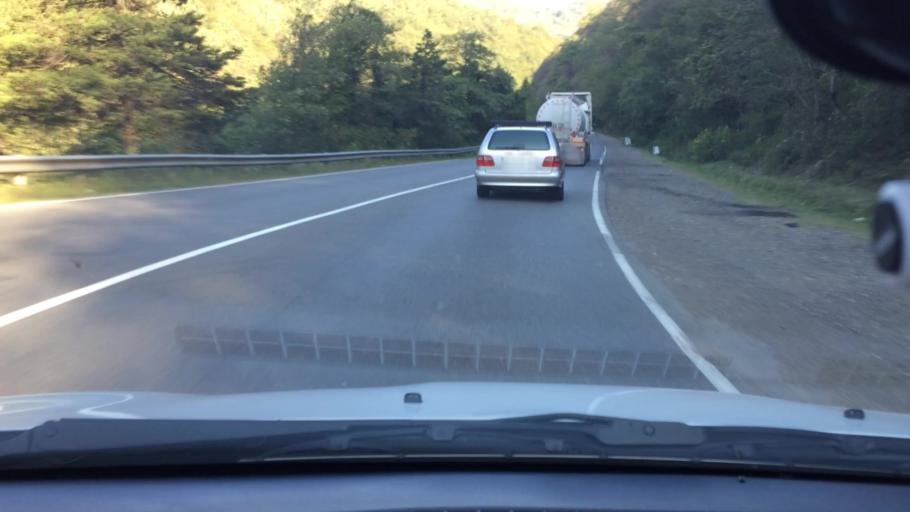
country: GE
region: Imereti
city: Kharagauli
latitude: 42.1046
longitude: 43.2064
